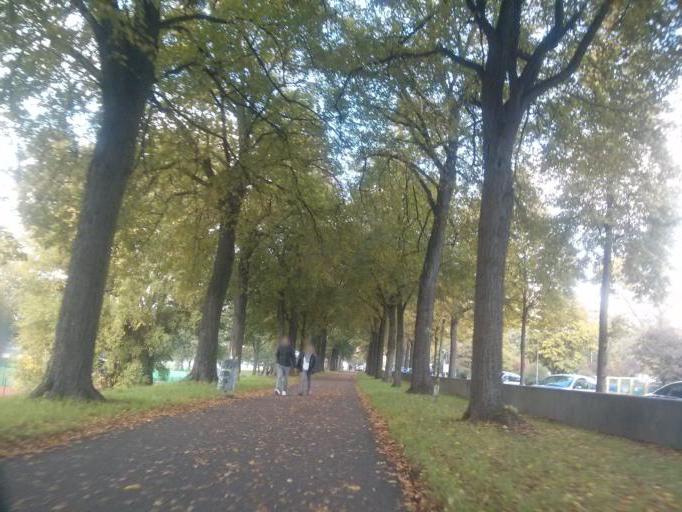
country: DE
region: North Rhine-Westphalia
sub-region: Regierungsbezirk Koln
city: Poll
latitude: 50.9167
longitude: 6.9796
